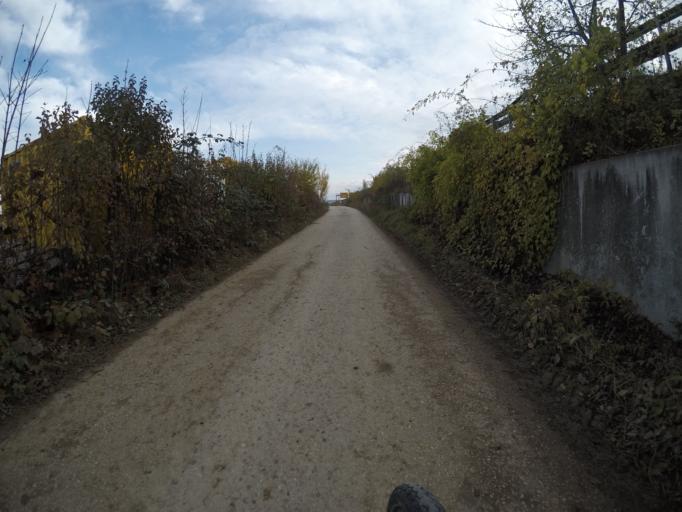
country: DE
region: Baden-Wuerttemberg
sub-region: Regierungsbezirk Stuttgart
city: Leinfelden-Echterdingen
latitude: 48.6981
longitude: 9.1687
